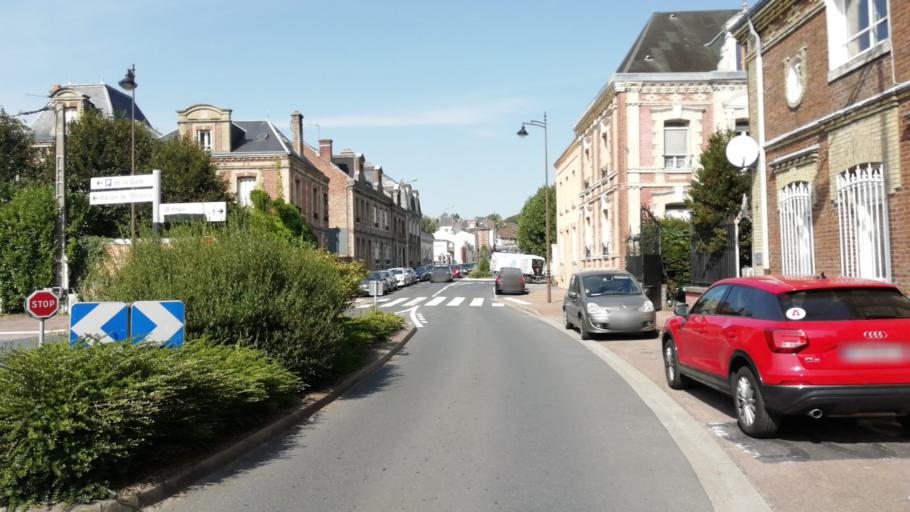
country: FR
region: Haute-Normandie
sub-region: Departement de la Seine-Maritime
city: Montivilliers
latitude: 49.5435
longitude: 0.1897
